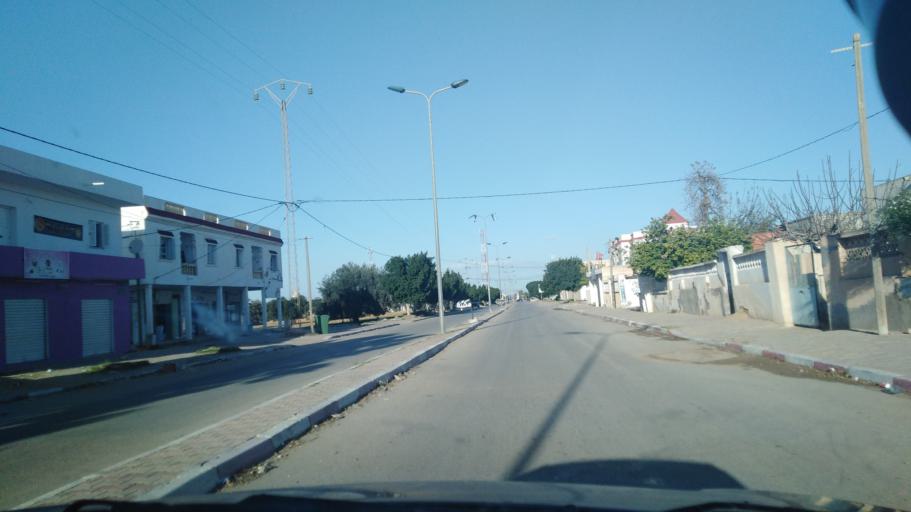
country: TN
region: Al Mahdiyah
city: Shurban
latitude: 34.9674
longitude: 10.3690
